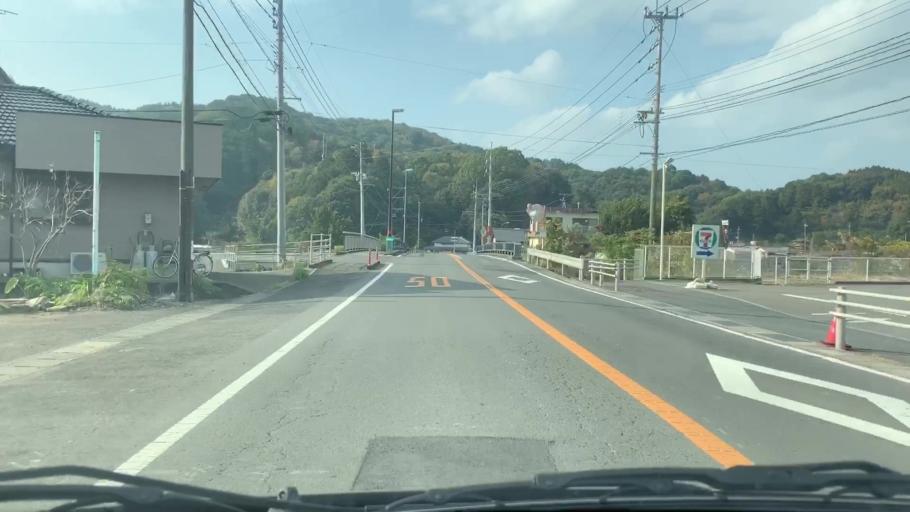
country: JP
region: Nagasaki
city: Sasebo
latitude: 32.9877
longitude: 129.7401
